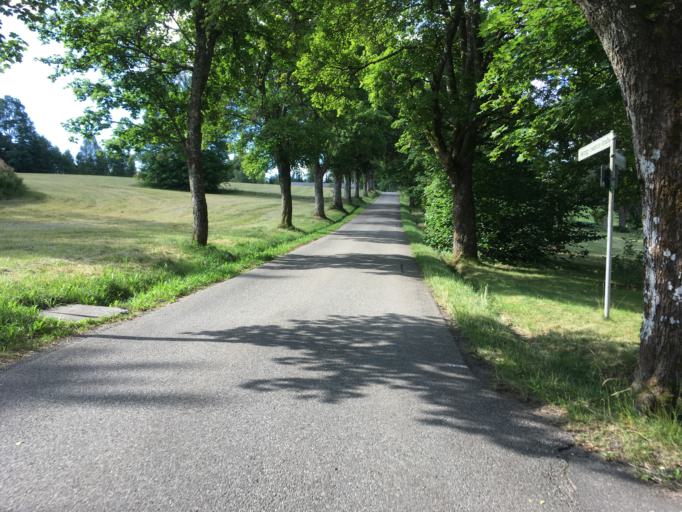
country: DE
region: Baden-Wuerttemberg
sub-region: Karlsruhe Region
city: Freudenstadt
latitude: 48.4560
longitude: 8.4094
